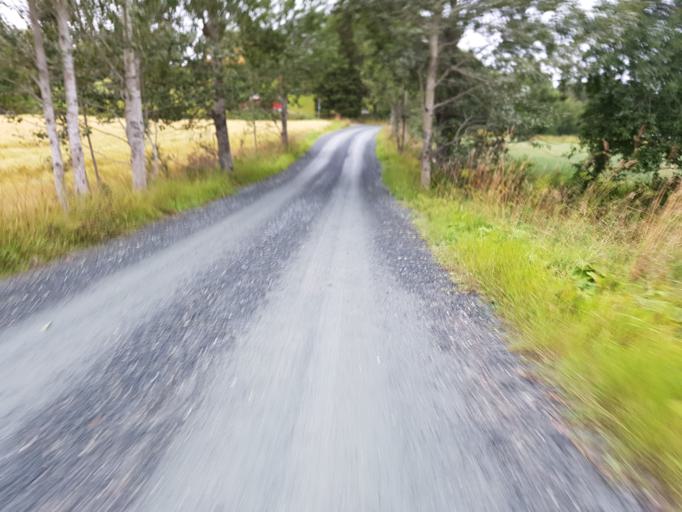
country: NO
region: Sor-Trondelag
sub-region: Trondheim
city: Trondheim
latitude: 63.4007
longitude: 10.4627
